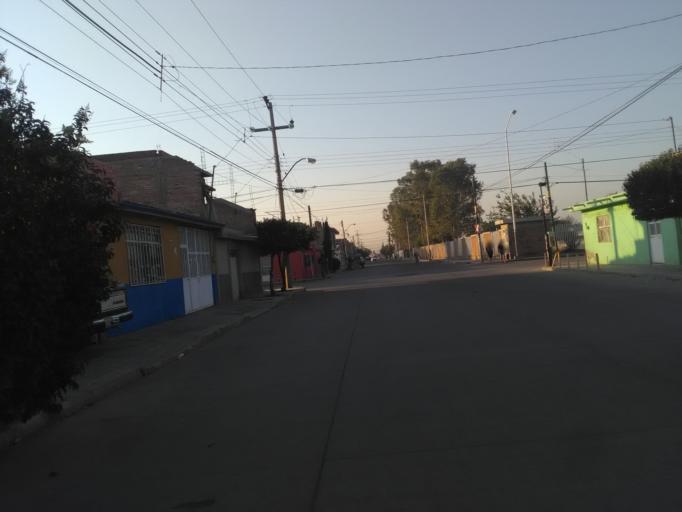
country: MX
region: Durango
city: Victoria de Durango
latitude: 24.0497
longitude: -104.6463
